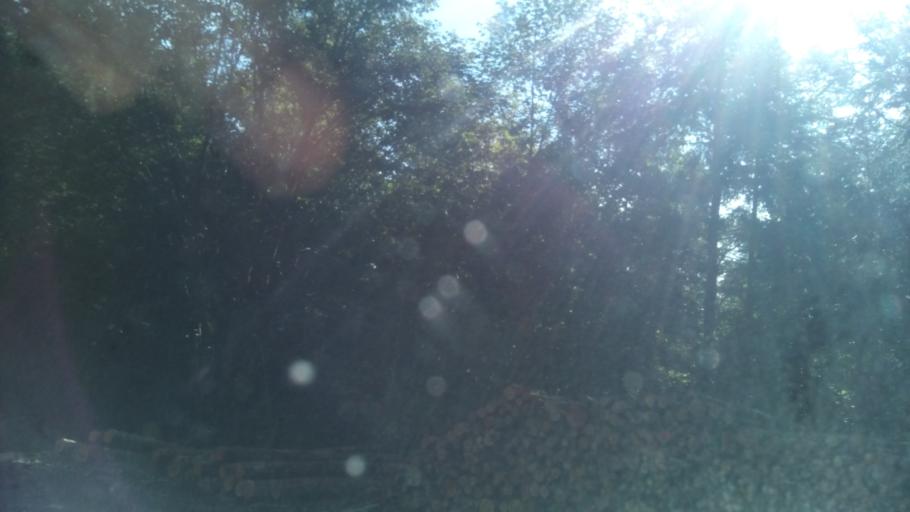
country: FR
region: Rhone-Alpes
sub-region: Departement du Rhone
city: Beaujeu
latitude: 46.1979
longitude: 4.5057
